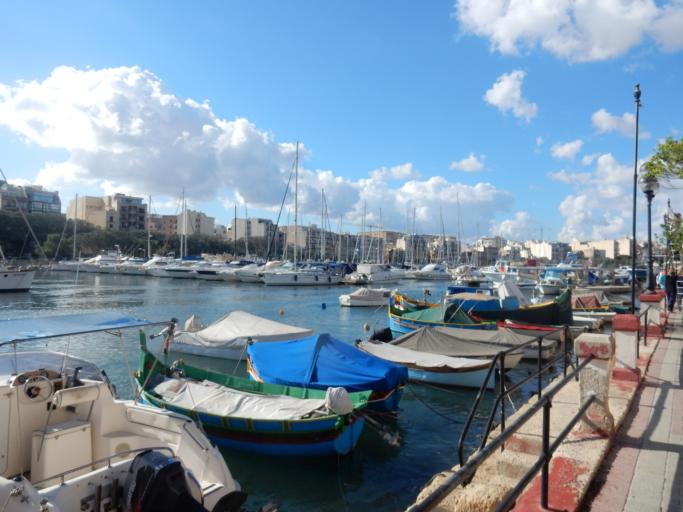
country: MT
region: Ta' Xbiex
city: Ta' Xbiex
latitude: 35.8971
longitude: 14.4934
